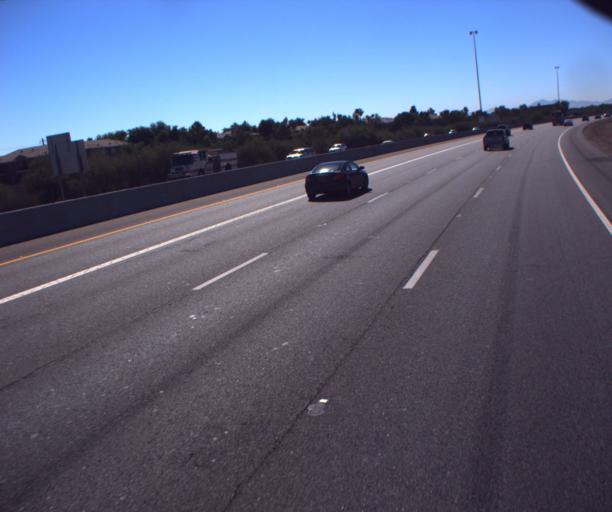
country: US
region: Arizona
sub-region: Maricopa County
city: Peoria
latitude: 33.6178
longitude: -112.2395
